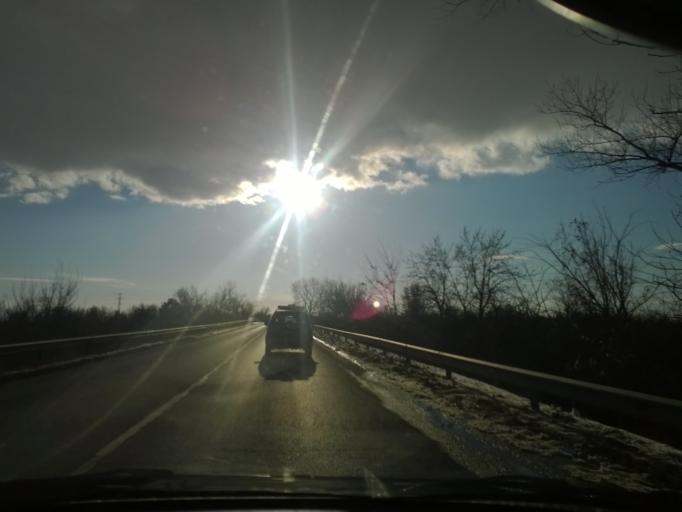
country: HU
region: Fejer
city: Polgardi
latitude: 47.0790
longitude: 18.3208
